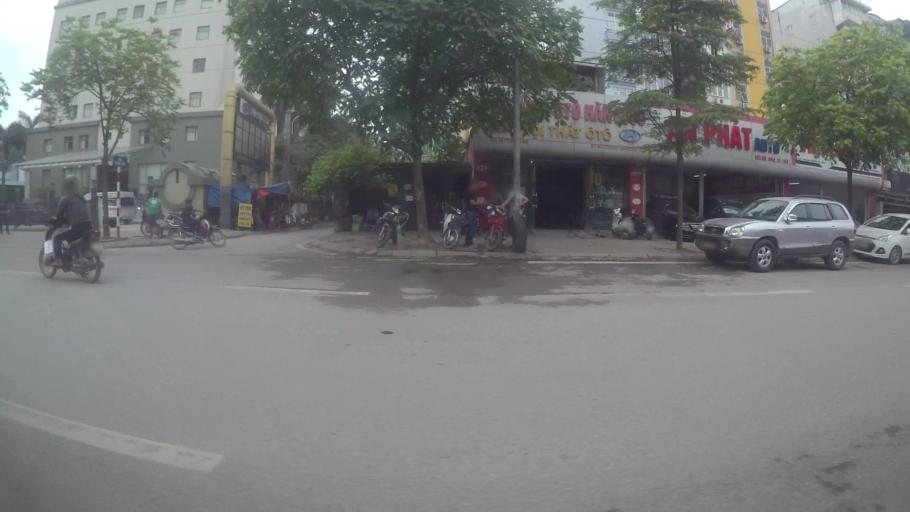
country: VN
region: Ha Noi
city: Cau Dien
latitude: 21.0204
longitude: 105.7796
